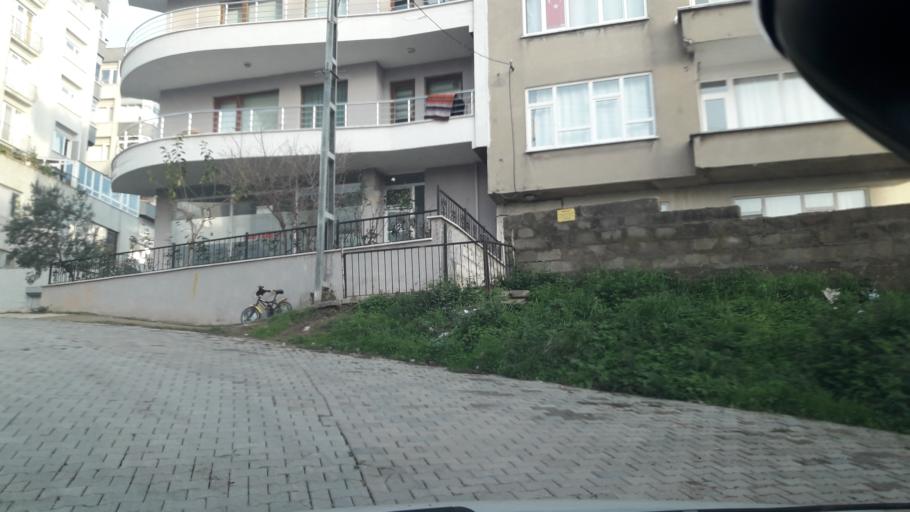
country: TR
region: Sinop
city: Sinop
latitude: 42.0273
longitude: 35.1580
